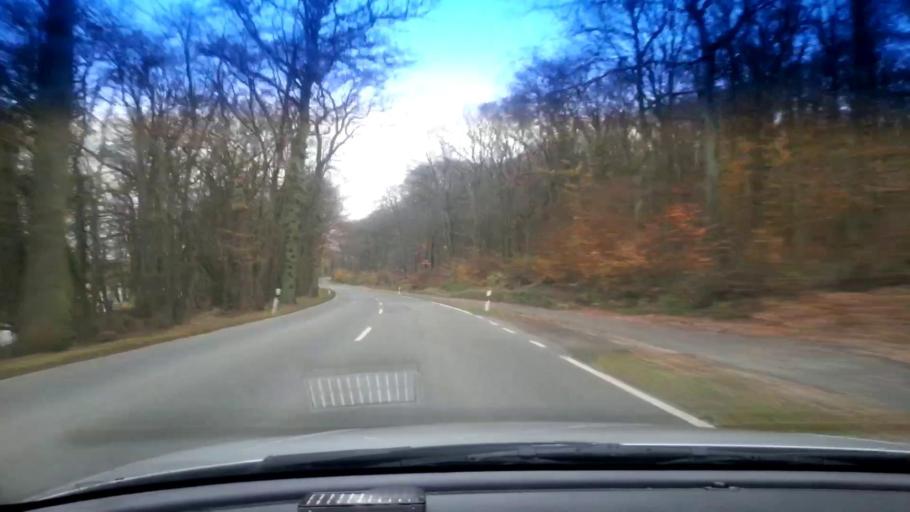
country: DE
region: Bavaria
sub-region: Upper Franconia
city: Pettstadt
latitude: 49.8524
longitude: 10.9255
